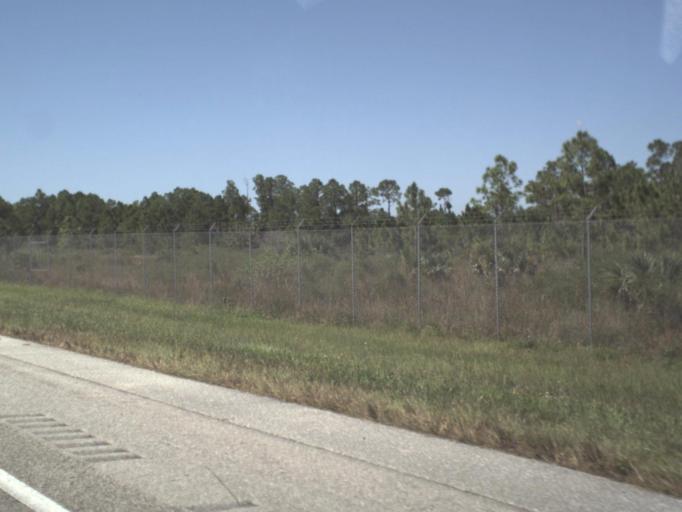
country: US
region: Florida
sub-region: Collier County
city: Orangetree
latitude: 26.1534
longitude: -81.4765
